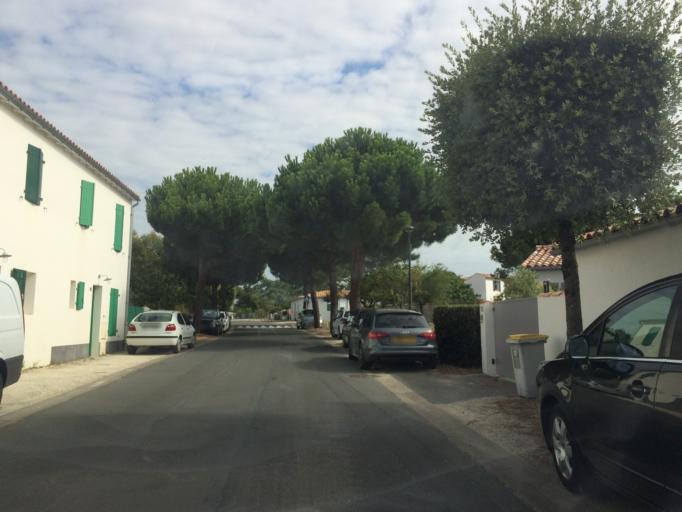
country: FR
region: Poitou-Charentes
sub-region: Departement de la Charente-Maritime
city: La Flotte
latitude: 46.1874
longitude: -1.3340
